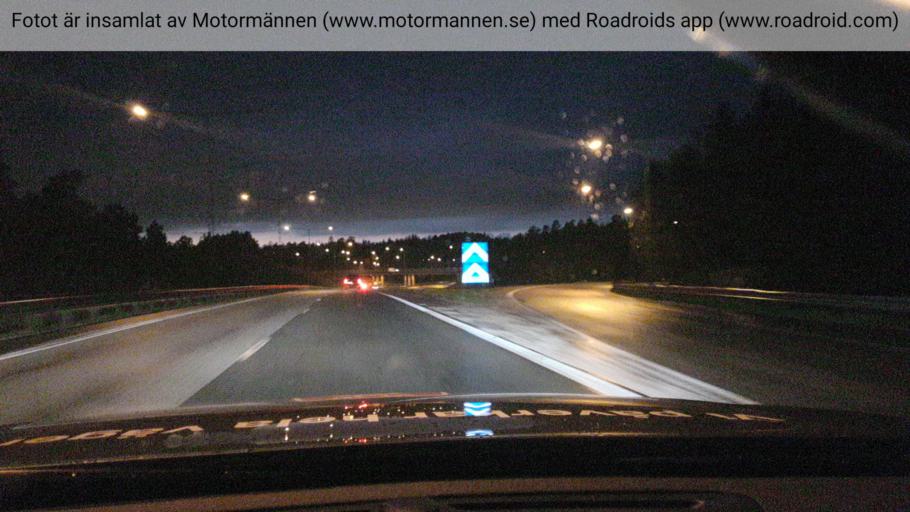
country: SE
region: Stockholm
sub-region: Nacka Kommun
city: Alta
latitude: 59.2489
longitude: 18.1745
